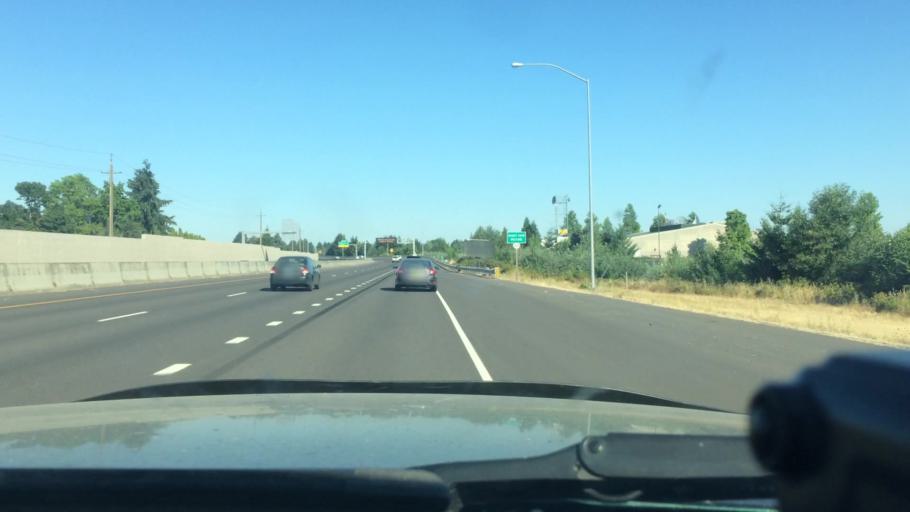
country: US
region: Oregon
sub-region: Lane County
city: Eugene
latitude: 44.0857
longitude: -123.0591
